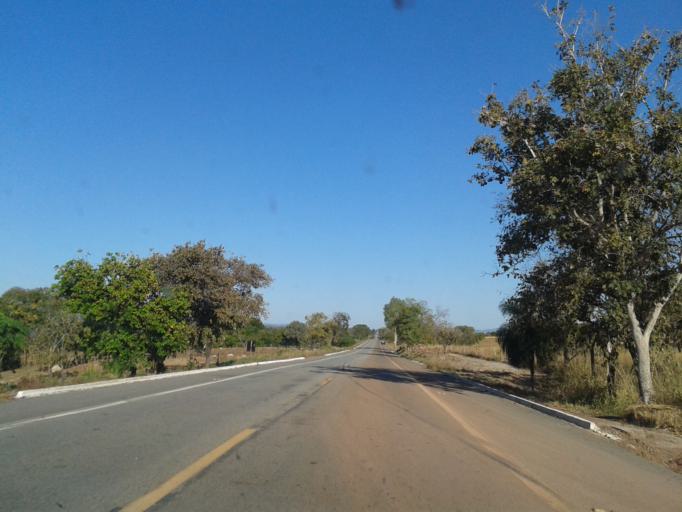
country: BR
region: Goias
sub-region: Mozarlandia
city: Mozarlandia
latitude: -15.2658
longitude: -50.4878
